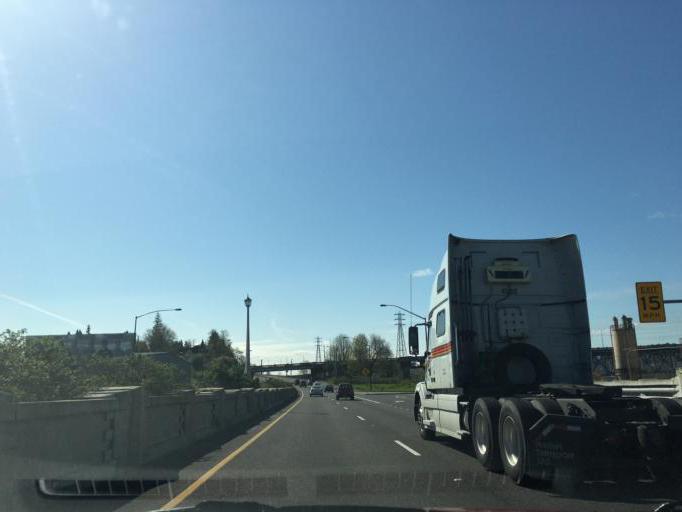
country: US
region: Oregon
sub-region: Multnomah County
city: Portland
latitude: 45.5040
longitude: -122.6609
